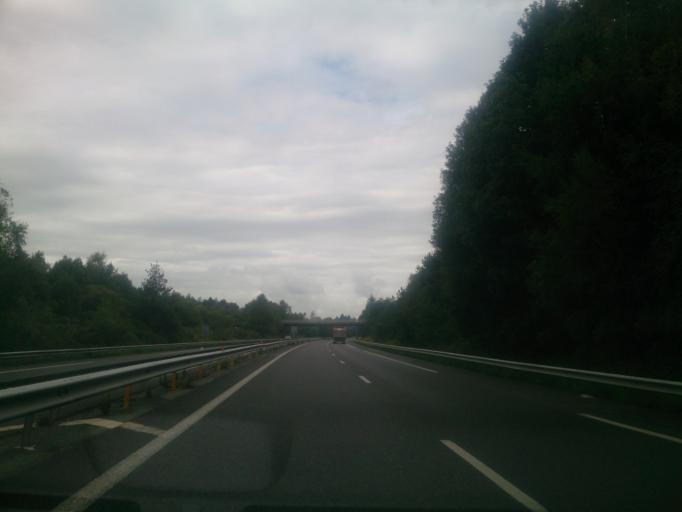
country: FR
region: Midi-Pyrenees
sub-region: Departement des Hautes-Pyrenees
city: La Barthe-de-Neste
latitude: 43.0992
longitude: 0.3996
